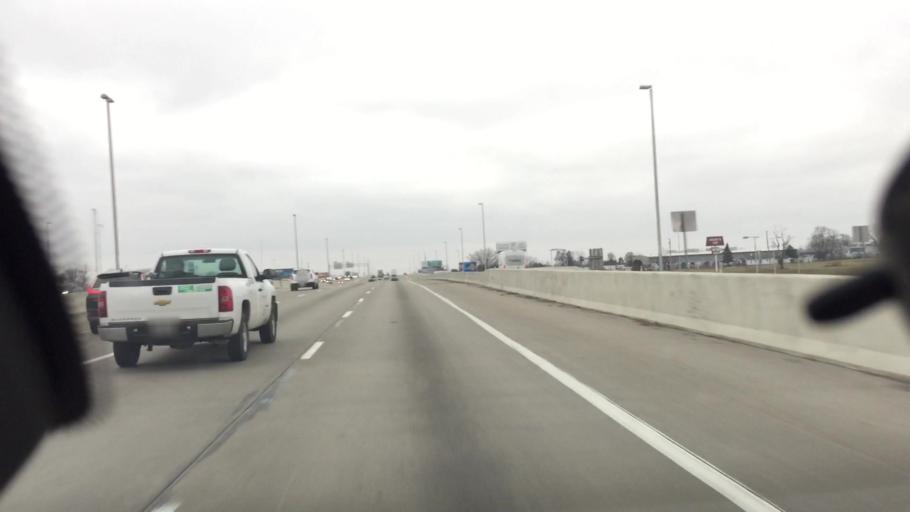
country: US
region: Indiana
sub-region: Marion County
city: Speedway
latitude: 39.7493
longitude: -86.2648
